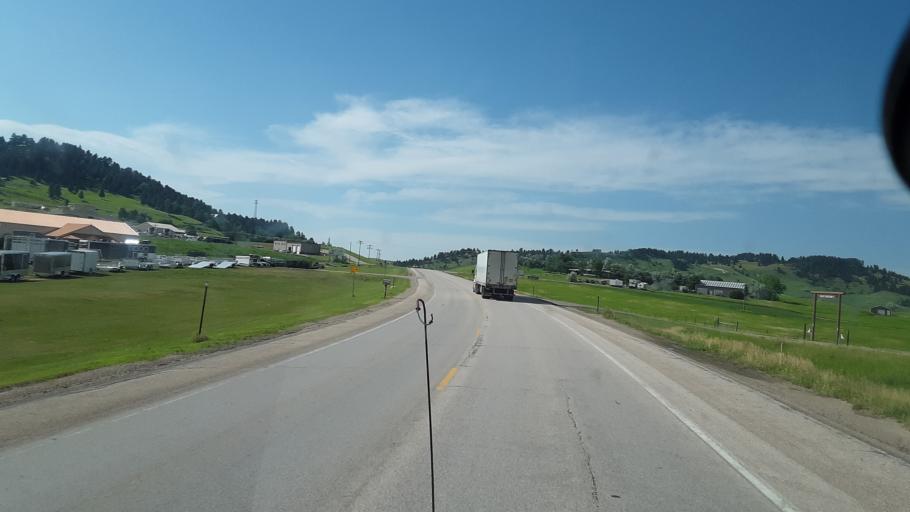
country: US
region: South Dakota
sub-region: Lawrence County
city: Deadwood
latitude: 44.4752
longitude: -103.6365
